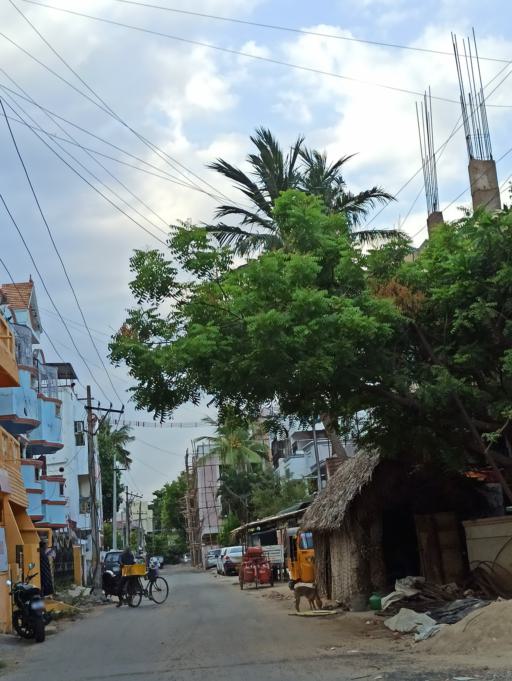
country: IN
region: Tamil Nadu
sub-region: Chennai
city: Chetput
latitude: 13.0579
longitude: 80.2065
